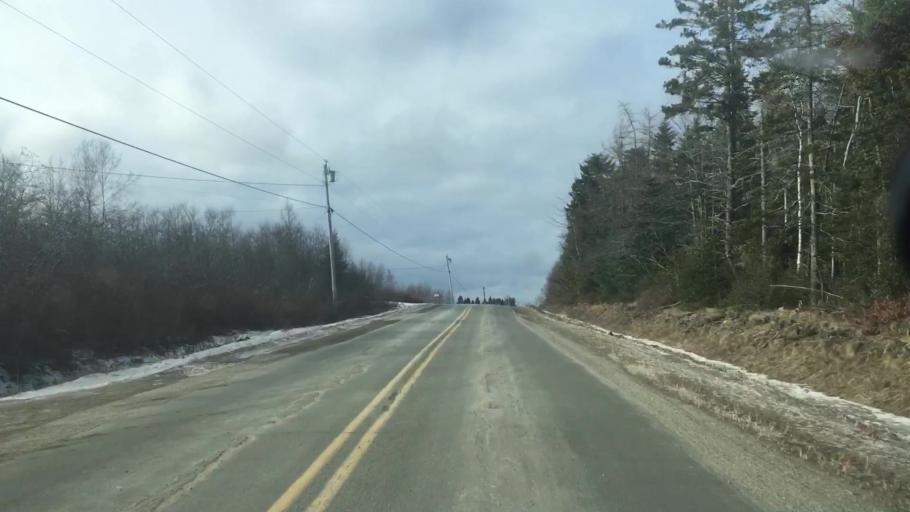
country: US
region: Maine
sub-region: Washington County
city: Machias
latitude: 44.6566
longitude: -67.5314
